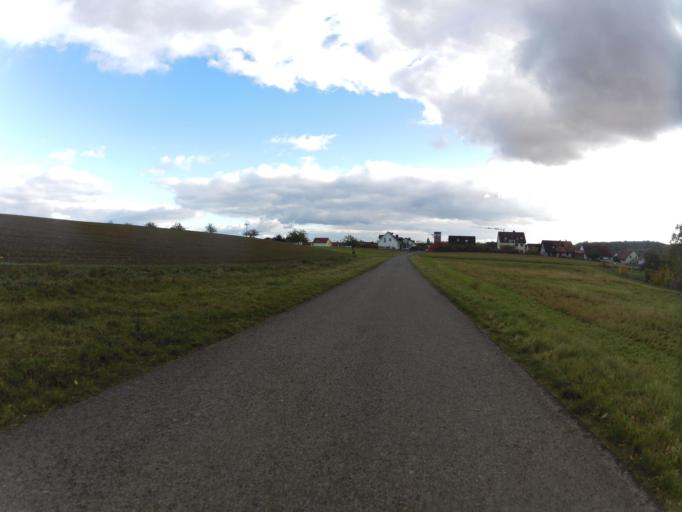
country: DE
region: Bavaria
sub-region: Regierungsbezirk Unterfranken
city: Kurnach
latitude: 49.8618
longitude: 10.0076
